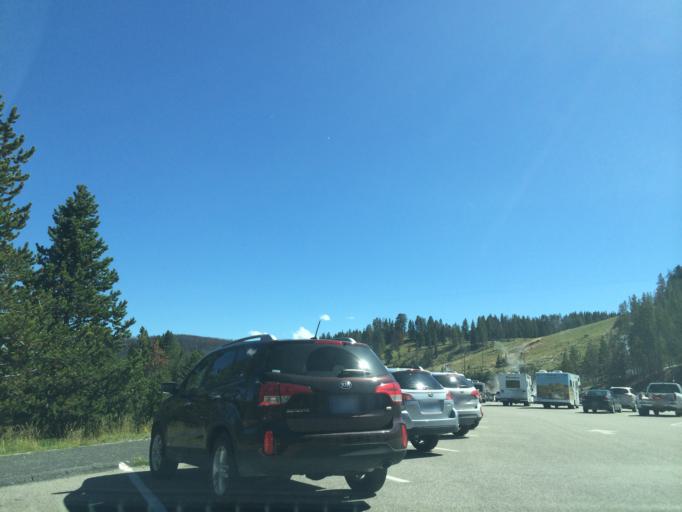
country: US
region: Montana
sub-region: Gallatin County
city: West Yellowstone
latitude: 44.6254
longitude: -110.4335
